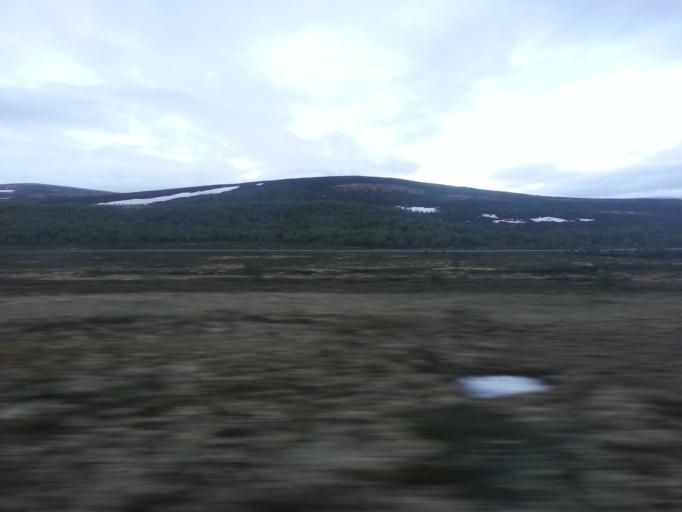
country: NO
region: Oppland
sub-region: Dovre
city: Dovre
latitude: 62.1059
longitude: 9.2500
